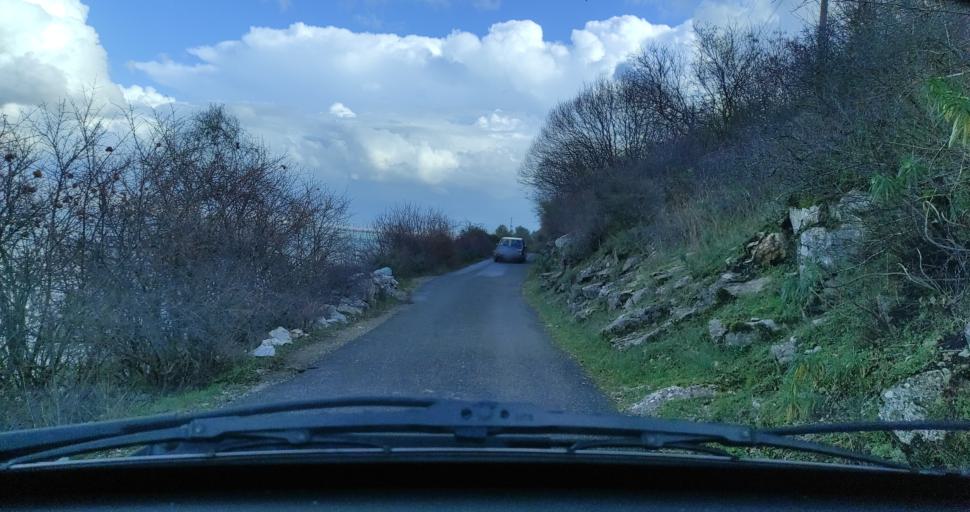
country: AL
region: Shkoder
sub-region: Rrethi i Shkodres
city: Dajc
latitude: 42.0694
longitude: 19.4070
